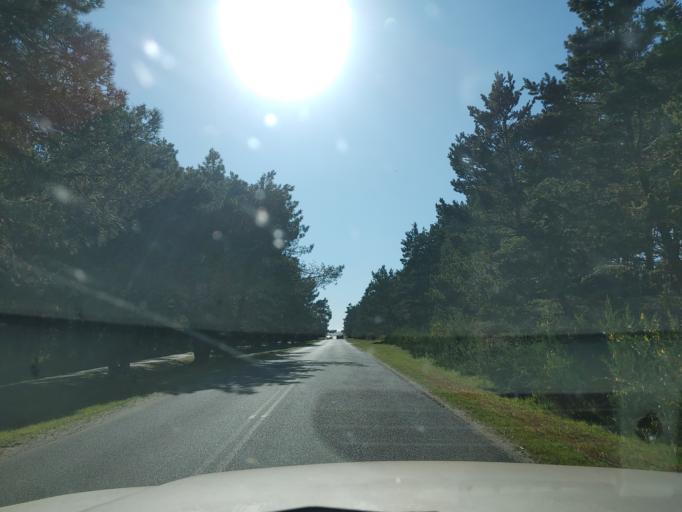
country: US
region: Oregon
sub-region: Clatsop County
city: Warrenton
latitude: 46.1792
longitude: -123.9745
